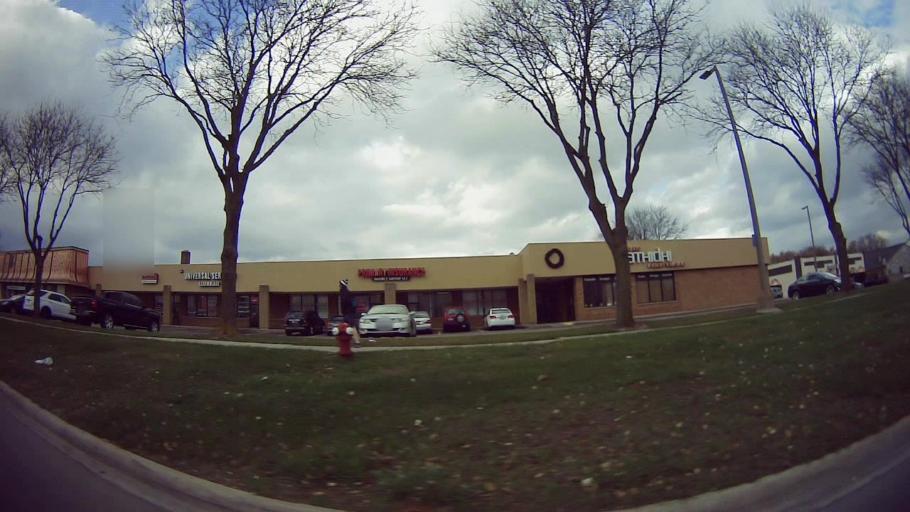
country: US
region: Michigan
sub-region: Oakland County
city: Clawson
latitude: 42.5495
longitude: -83.0876
